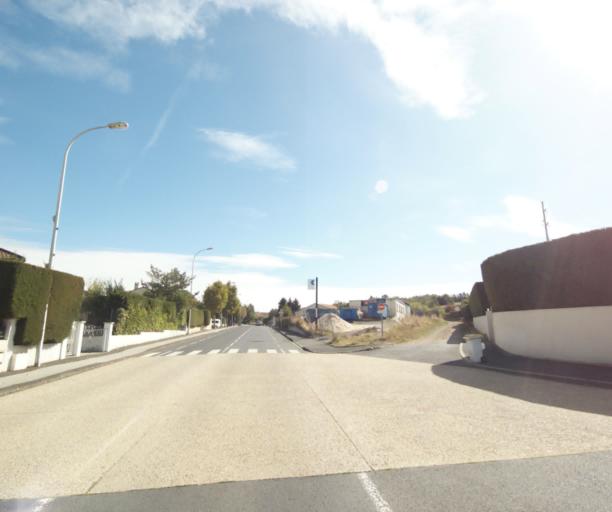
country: FR
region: Auvergne
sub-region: Departement du Puy-de-Dome
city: Cournon-d'Auvergne
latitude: 45.7650
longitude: 3.2012
